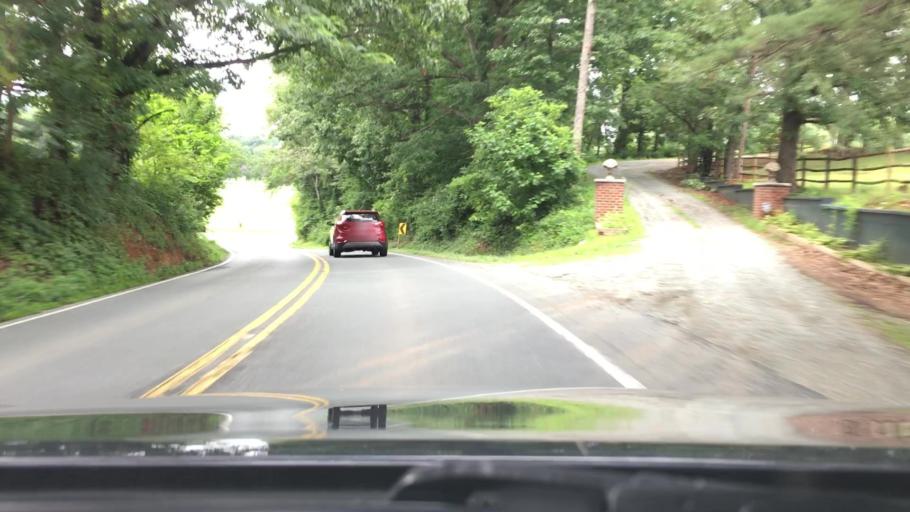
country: US
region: Virginia
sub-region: Fluvanna County
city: Lake Monticello
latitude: 38.0351
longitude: -78.3435
